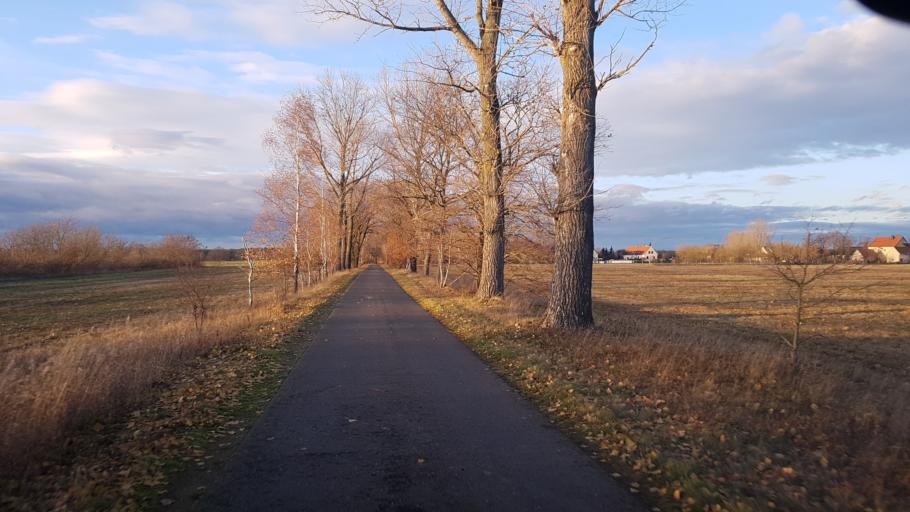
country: DE
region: Brandenburg
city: Falkenberg
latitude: 51.6385
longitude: 13.2639
